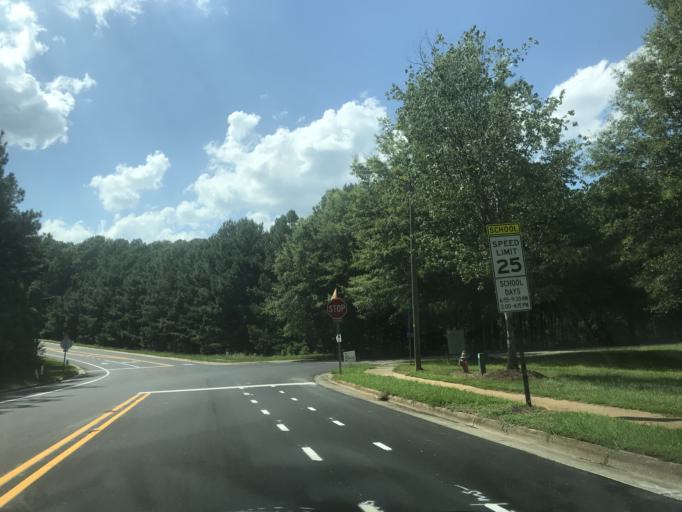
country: US
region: North Carolina
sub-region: Wake County
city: Cary
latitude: 35.8865
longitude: -78.7204
